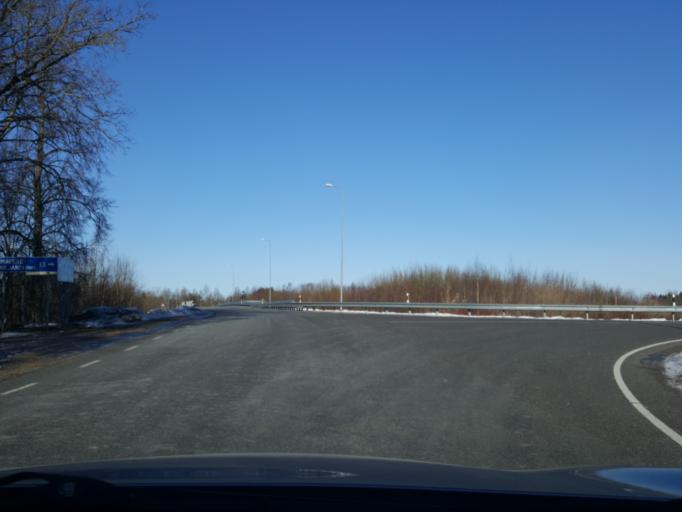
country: EE
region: Viljandimaa
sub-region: Vohma linn
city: Vohma
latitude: 58.5613
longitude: 25.5524
